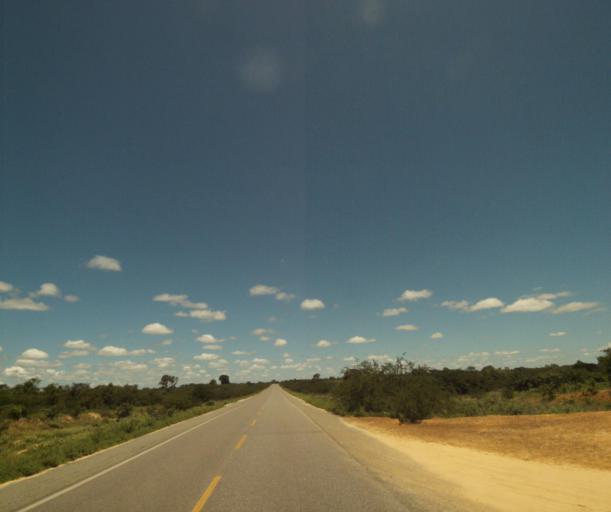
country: BR
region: Bahia
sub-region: Carinhanha
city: Carinhanha
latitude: -14.2984
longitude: -43.7854
